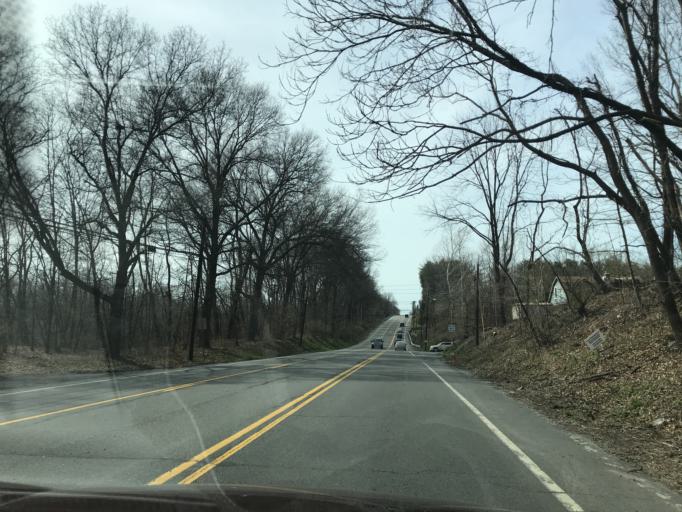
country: US
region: Pennsylvania
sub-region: Northumberland County
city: Northumberland
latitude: 40.8965
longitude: -76.8138
